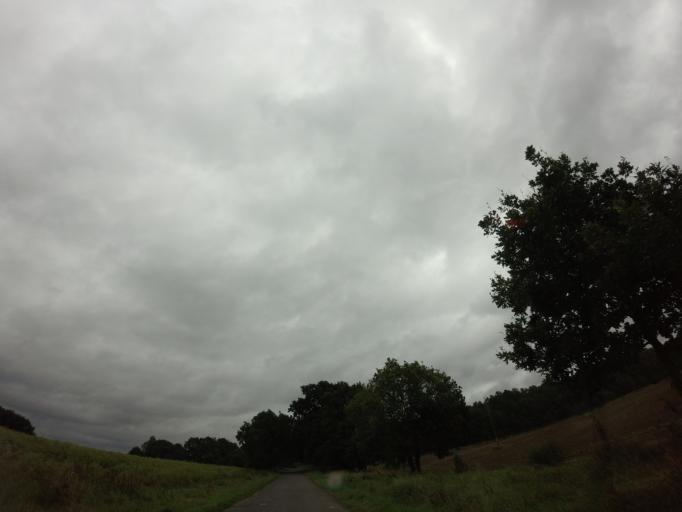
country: PL
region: West Pomeranian Voivodeship
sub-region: Powiat choszczenski
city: Choszczno
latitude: 53.1622
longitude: 15.3765
